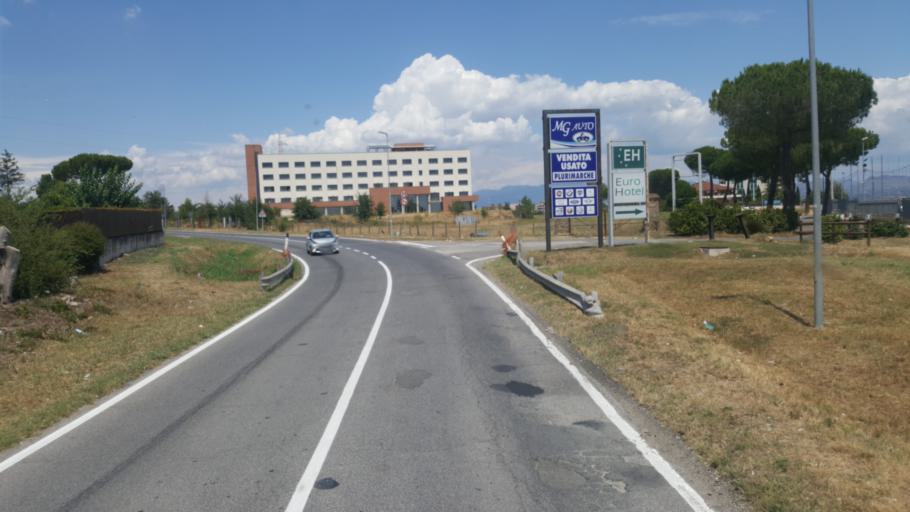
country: IT
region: Latium
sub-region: Citta metropolitana di Roma Capitale
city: Bivio di Capanelle
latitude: 42.1340
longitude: 12.5980
